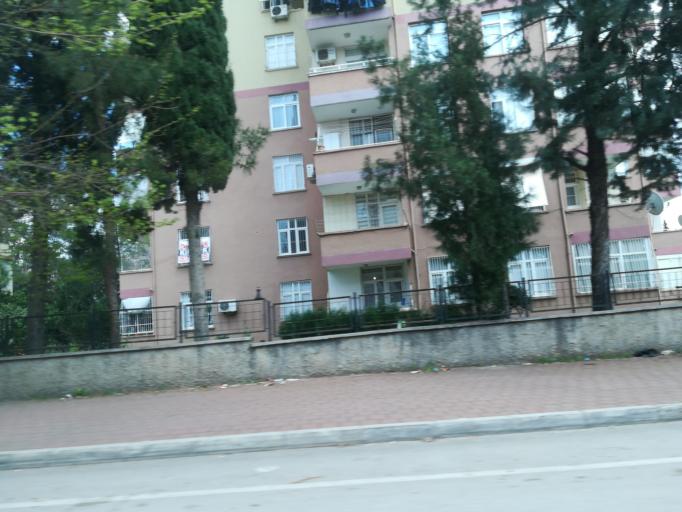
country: TR
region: Adana
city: Adana
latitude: 37.0355
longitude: 35.3126
